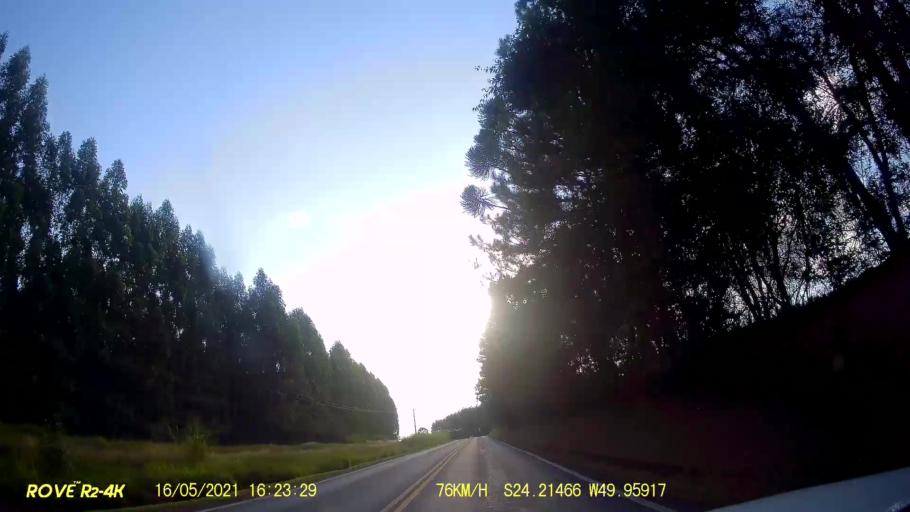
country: BR
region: Parana
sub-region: Jaguariaiva
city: Jaguariaiva
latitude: -24.2143
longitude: -49.9590
